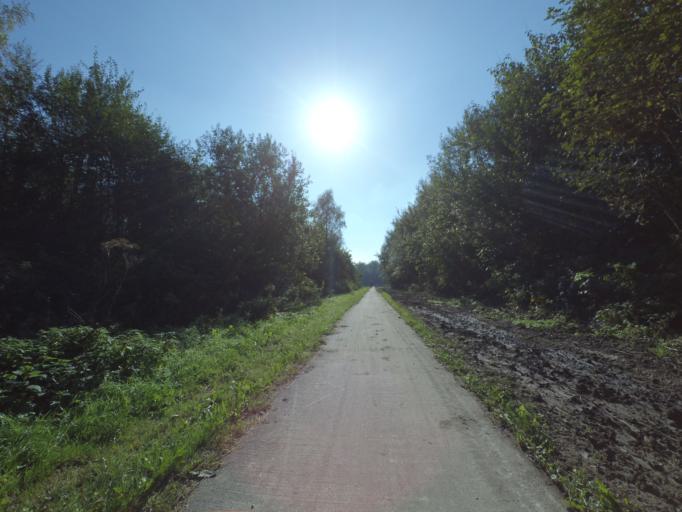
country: NL
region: Flevoland
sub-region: Gemeente Zeewolde
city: Zeewolde
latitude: 52.3024
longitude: 5.5239
